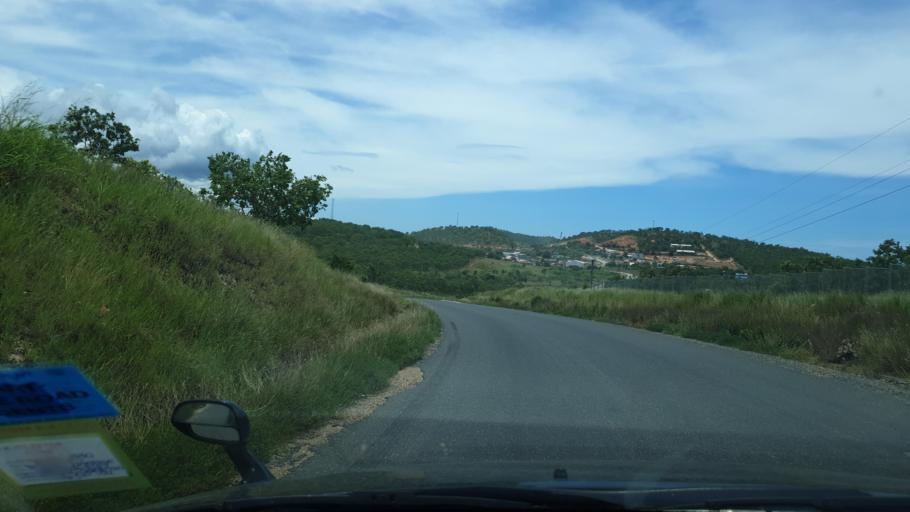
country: PG
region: National Capital
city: Port Moresby
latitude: -9.4422
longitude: 147.0763
